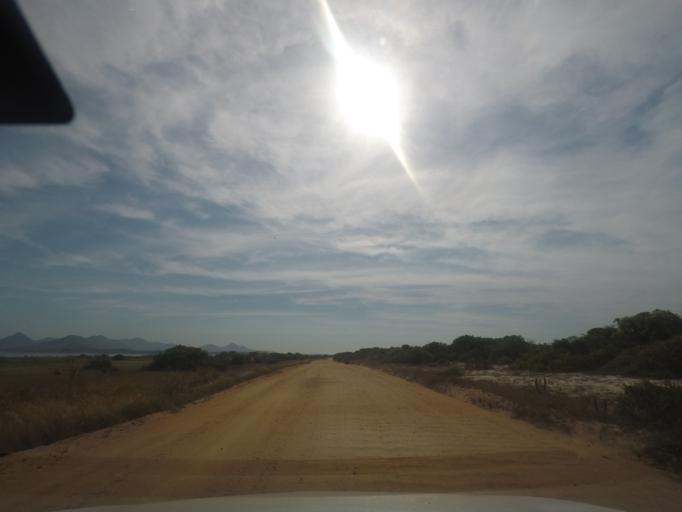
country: BR
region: Rio de Janeiro
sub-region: Marica
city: Marica
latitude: -22.9599
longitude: -42.8689
